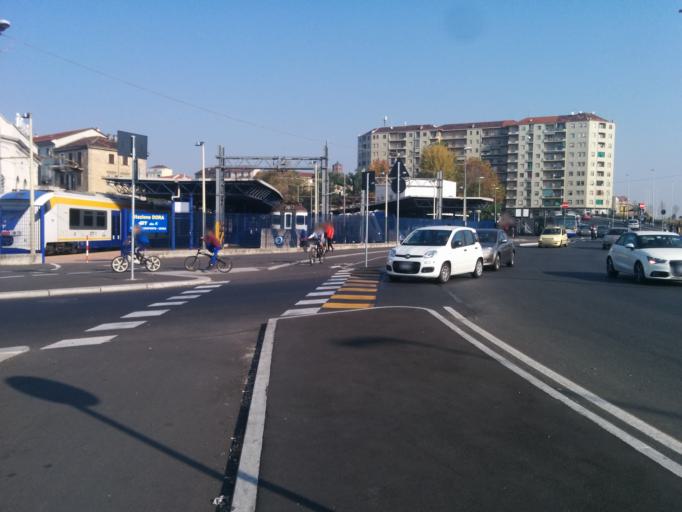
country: IT
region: Piedmont
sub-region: Provincia di Torino
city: Turin
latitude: 45.0900
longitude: 7.6771
